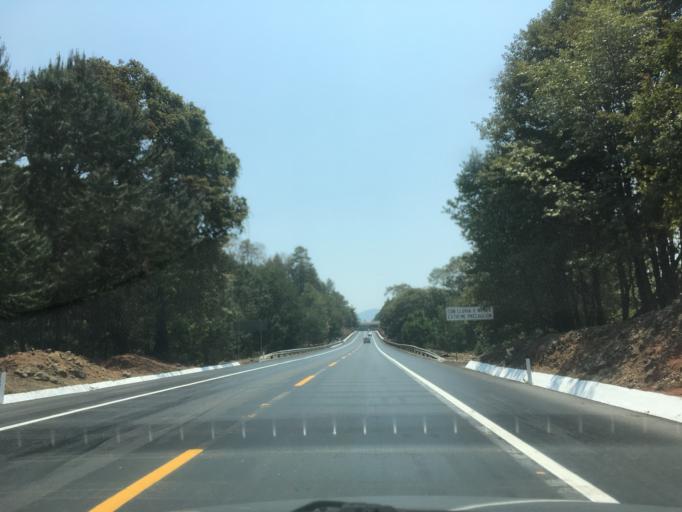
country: MX
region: Michoacan
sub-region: Patzcuaro
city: Santa Maria Huiramangaro (San Juan Tumbio)
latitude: 19.4886
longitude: -101.7159
